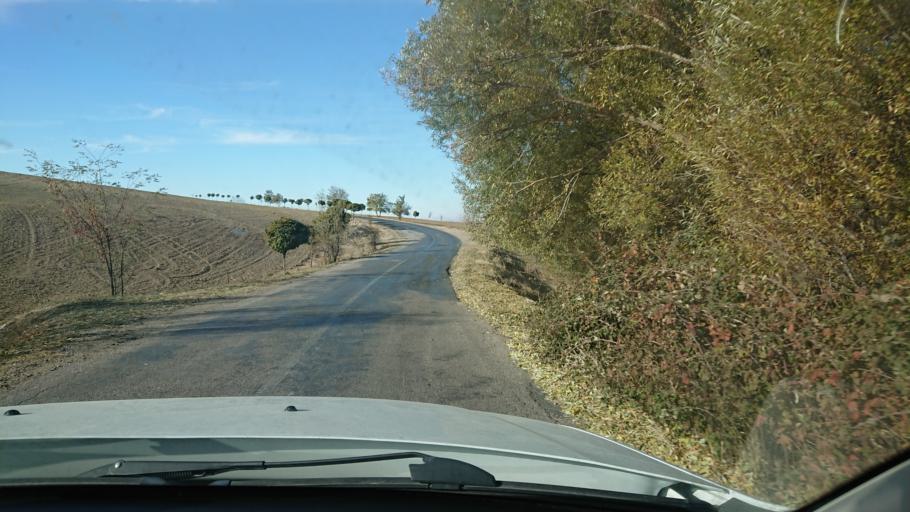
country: TR
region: Aksaray
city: Sariyahsi
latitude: 38.9703
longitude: 33.8666
